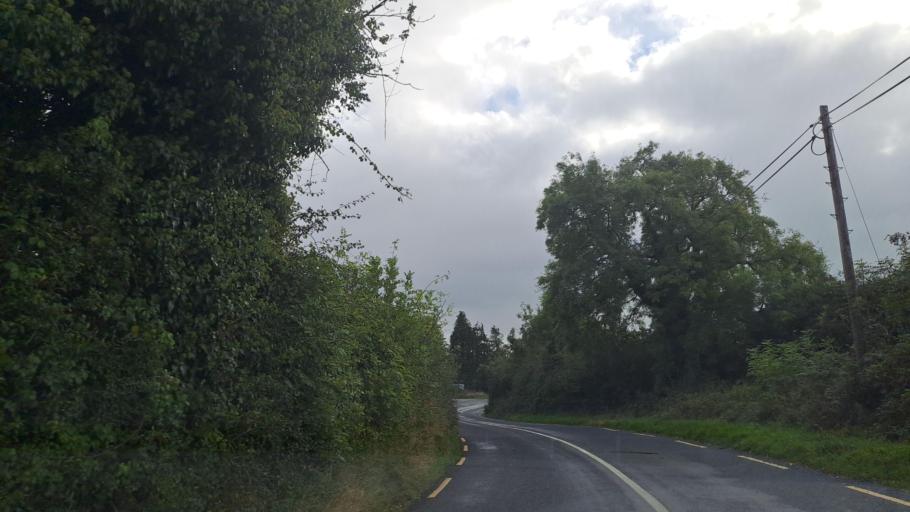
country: IE
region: Ulster
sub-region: County Monaghan
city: Carrickmacross
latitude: 53.9987
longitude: -6.7187
